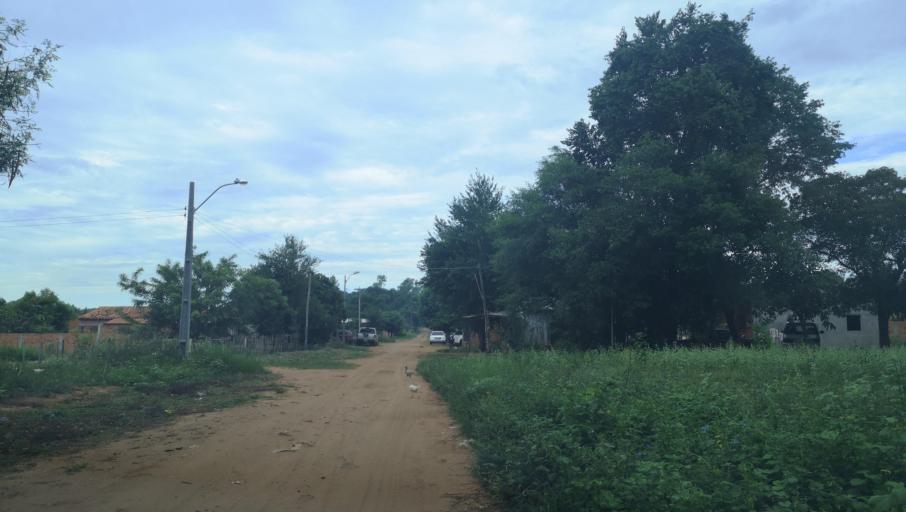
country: PY
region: San Pedro
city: Capiibary
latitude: -24.7353
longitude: -56.0236
